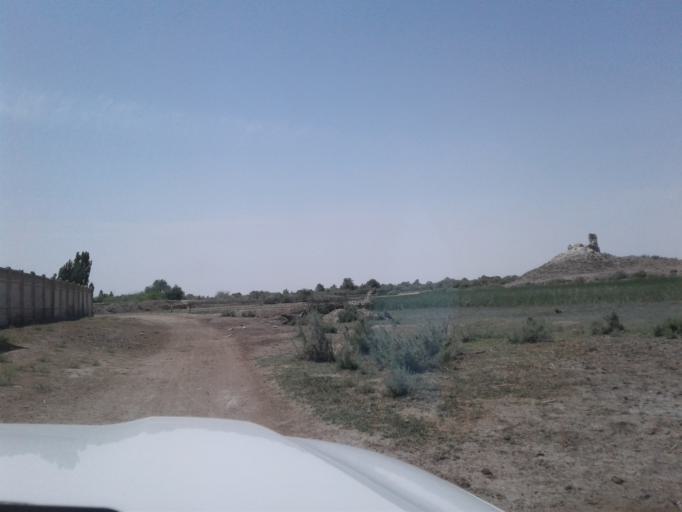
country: TM
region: Dasoguz
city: Tagta
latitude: 41.5418
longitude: 60.0025
